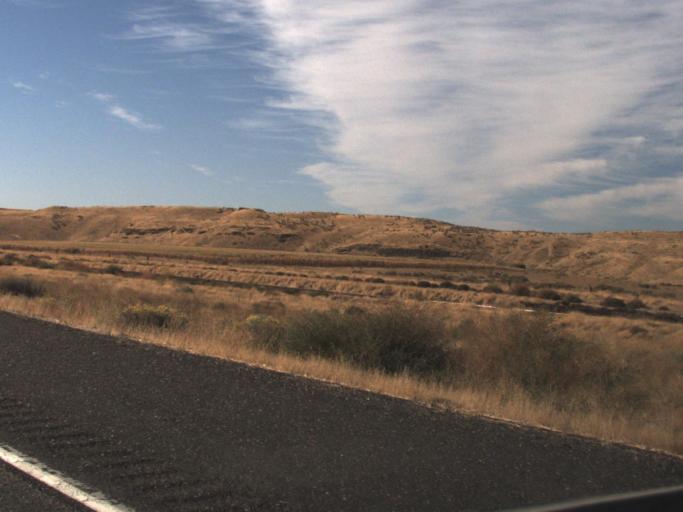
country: US
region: Washington
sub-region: Franklin County
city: Basin City
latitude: 46.5344
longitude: -119.0148
